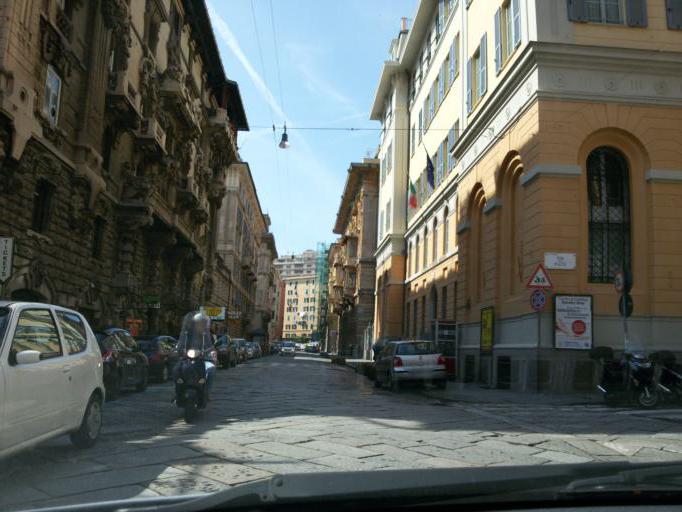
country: IT
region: Liguria
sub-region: Provincia di Genova
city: San Teodoro
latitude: 44.4051
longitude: 8.9412
